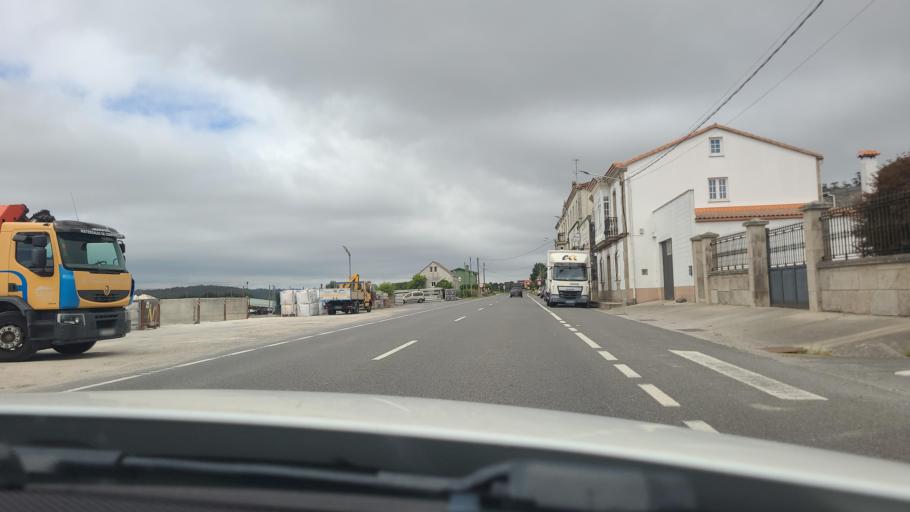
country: ES
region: Galicia
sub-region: Provincia da Coruna
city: Cee
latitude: 42.9886
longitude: -9.1841
